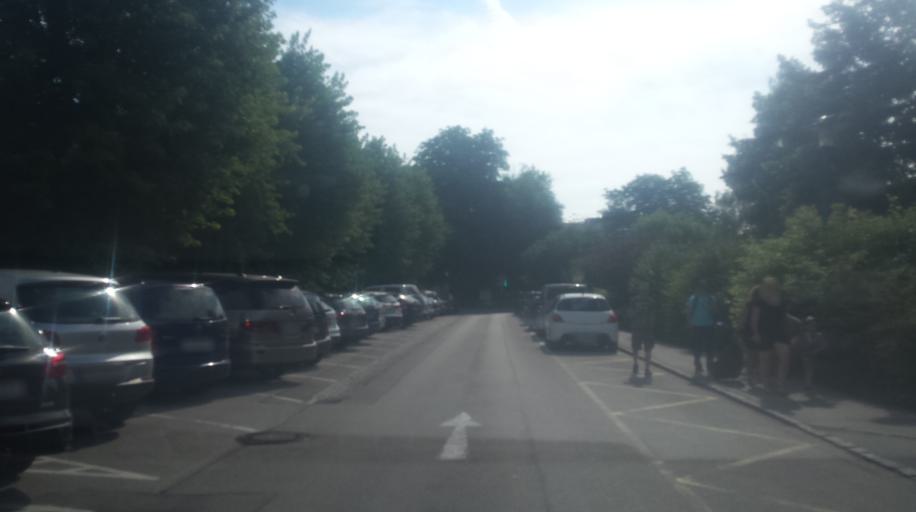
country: AT
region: Upper Austria
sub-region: Politischer Bezirk Grieskirchen
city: Bad Schallerbach
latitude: 48.2267
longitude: 13.9191
